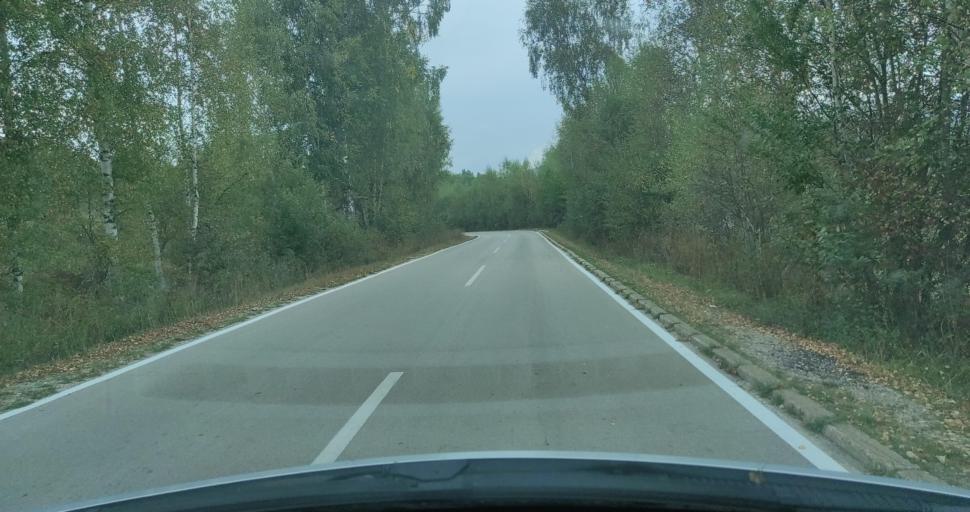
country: RS
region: Central Serbia
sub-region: Jablanicki Okrug
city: Crna Trava
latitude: 42.7368
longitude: 22.3308
